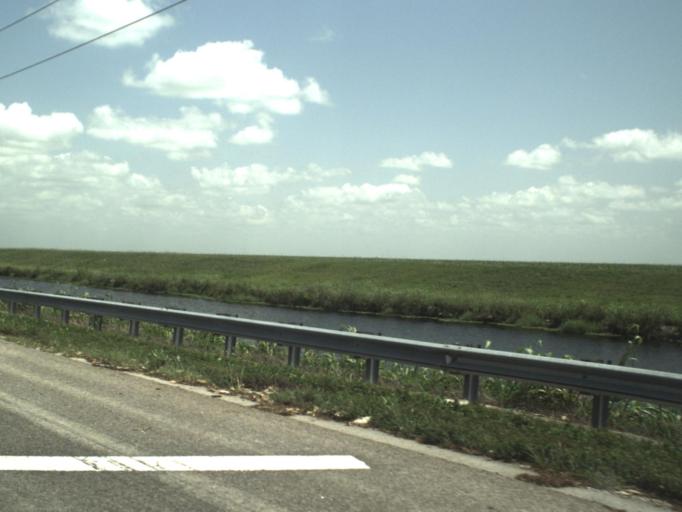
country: US
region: Florida
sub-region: Palm Beach County
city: Belle Glade Camp
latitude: 26.5881
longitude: -80.7109
